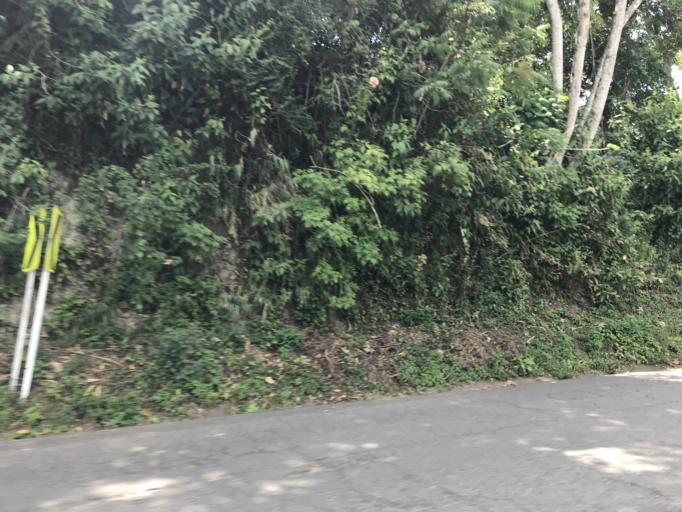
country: CO
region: Huila
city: San Agustin
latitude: 1.8755
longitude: -76.2497
